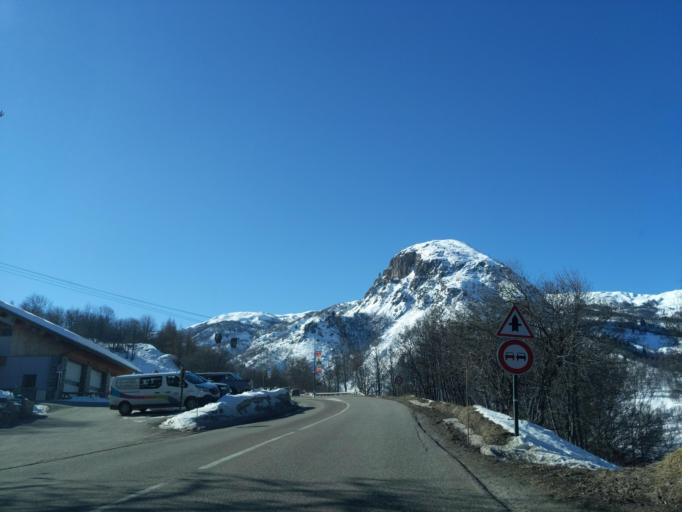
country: FR
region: Rhone-Alpes
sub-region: Departement de la Savoie
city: Saint-Martin-de-Belleville
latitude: 45.3773
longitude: 6.5077
